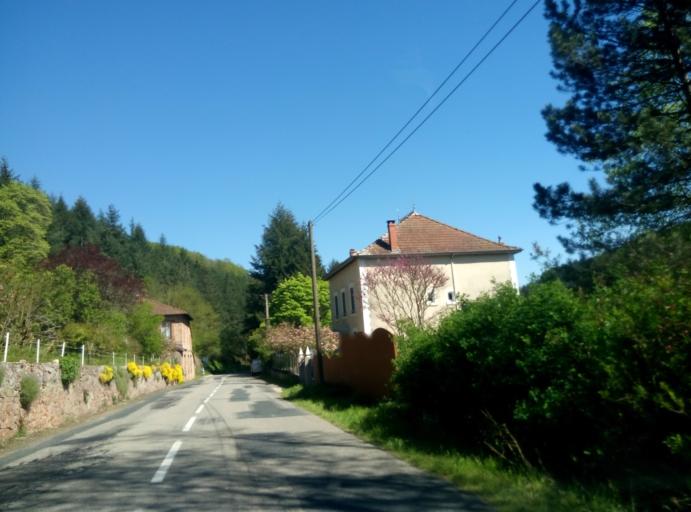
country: FR
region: Rhone-Alpes
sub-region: Departement du Rhone
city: Grandris
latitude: 46.0040
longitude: 4.4746
